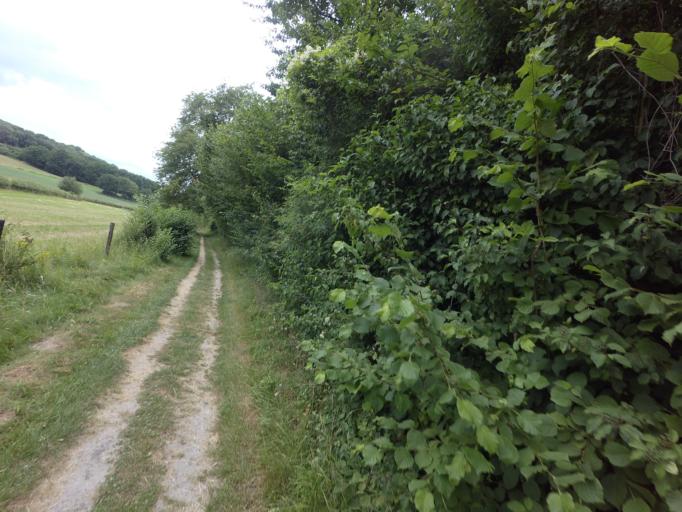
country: NL
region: Limburg
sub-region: Valkenburg aan de Geul
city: Schin op Geul
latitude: 50.8439
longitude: 5.8566
